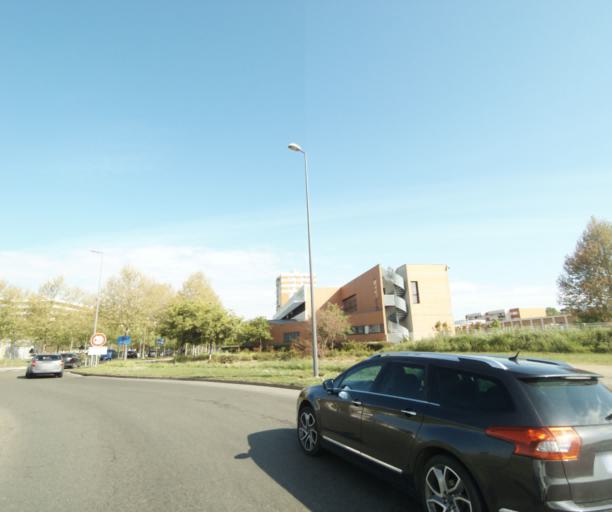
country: FR
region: Ile-de-France
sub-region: Departement des Yvelines
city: Les Mureaux
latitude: 48.9750
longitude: 1.9167
